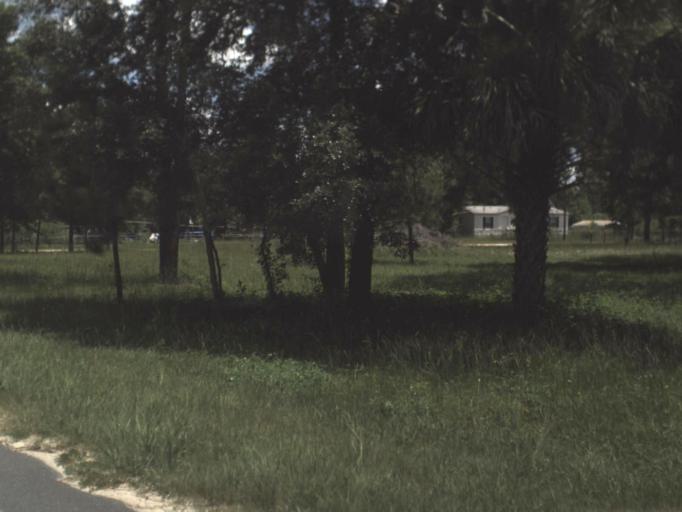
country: US
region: Florida
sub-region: Alachua County
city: Hawthorne
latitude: 29.6226
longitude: -82.0275
